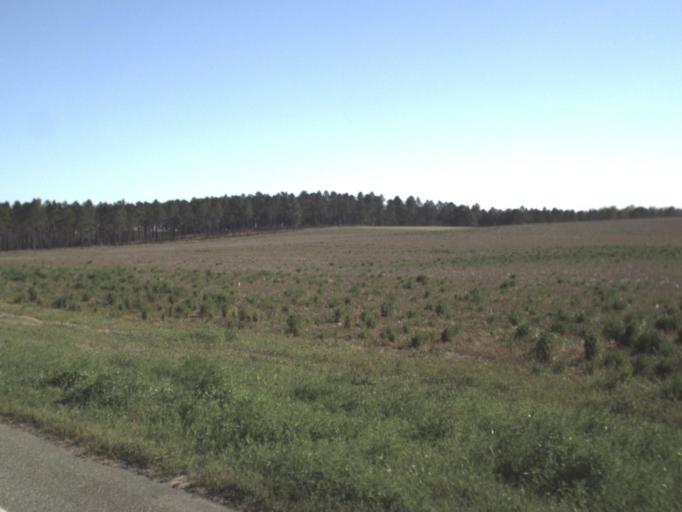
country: US
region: Georgia
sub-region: Brooks County
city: Quitman
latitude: 30.6225
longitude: -83.6468
